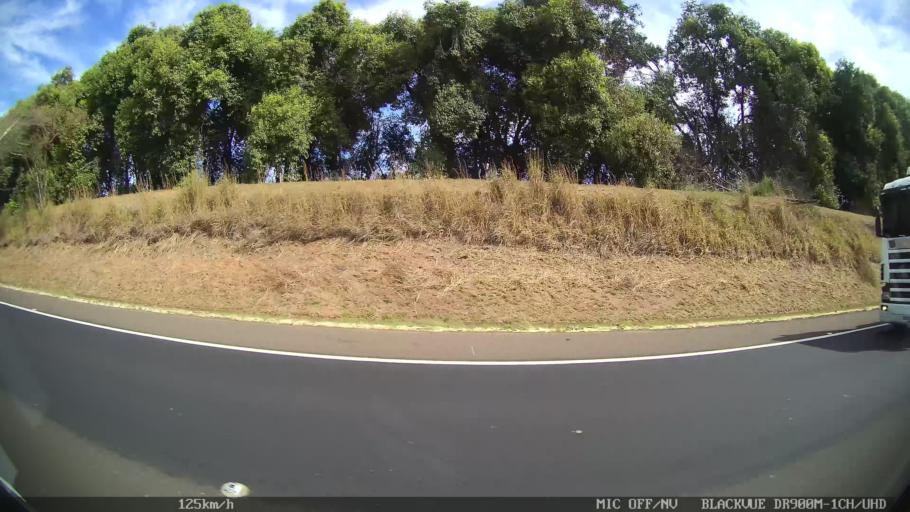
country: BR
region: Sao Paulo
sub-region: Matao
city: Matao
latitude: -21.6164
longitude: -48.4180
